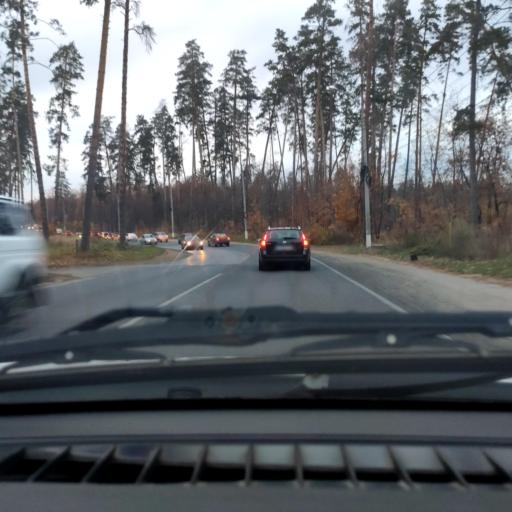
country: RU
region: Samara
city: Tol'yatti
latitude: 53.4911
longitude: 49.3058
